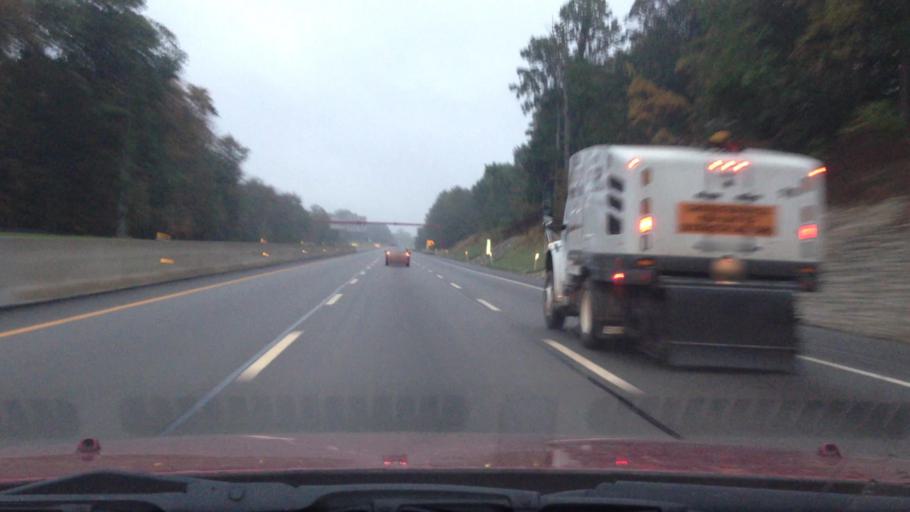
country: US
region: Pennsylvania
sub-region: Montgomery County
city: Dresher
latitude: 40.1458
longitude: -75.1540
